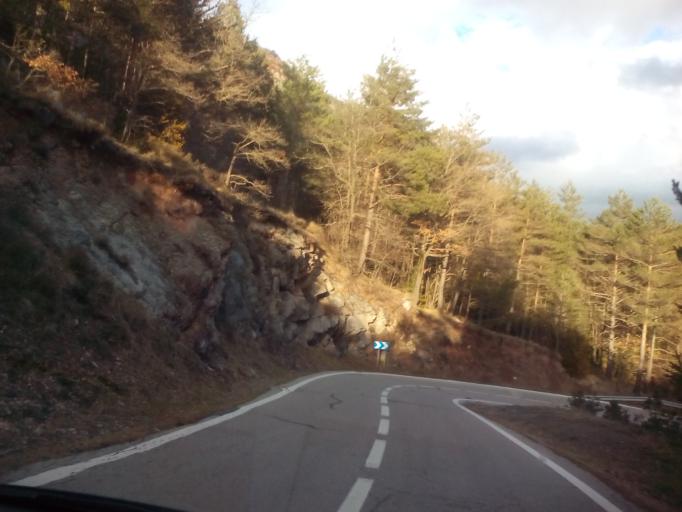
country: ES
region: Catalonia
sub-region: Provincia de Girona
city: Toses
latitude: 42.2630
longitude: 1.9862
